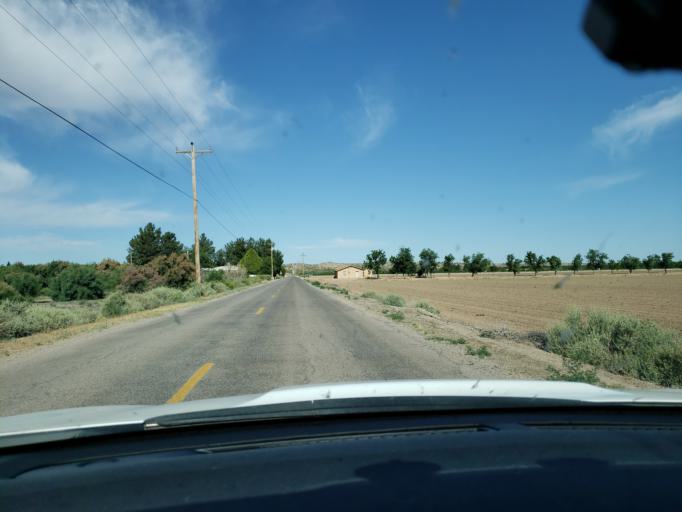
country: US
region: New Mexico
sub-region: Dona Ana County
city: Vado
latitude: 32.0826
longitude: -106.6947
